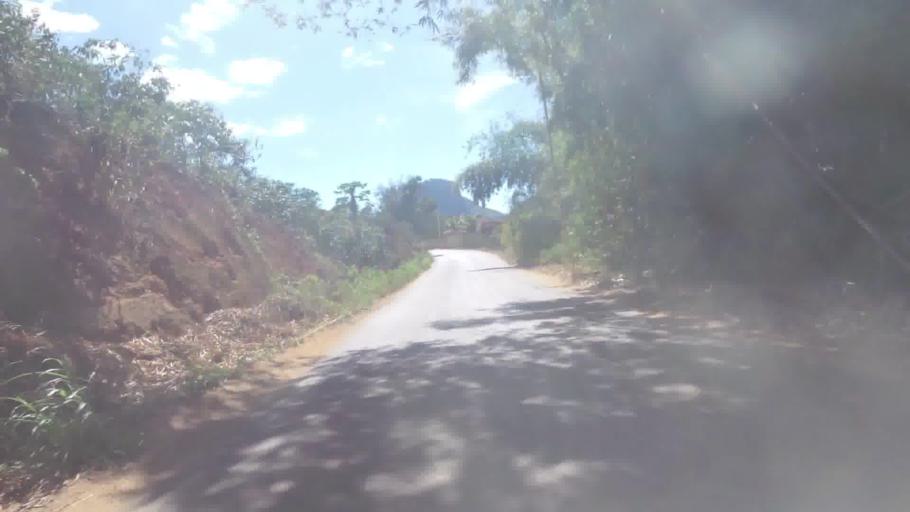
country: BR
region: Espirito Santo
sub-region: Cachoeiro De Itapemirim
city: Cachoeiro de Itapemirim
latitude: -20.9281
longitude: -41.2126
